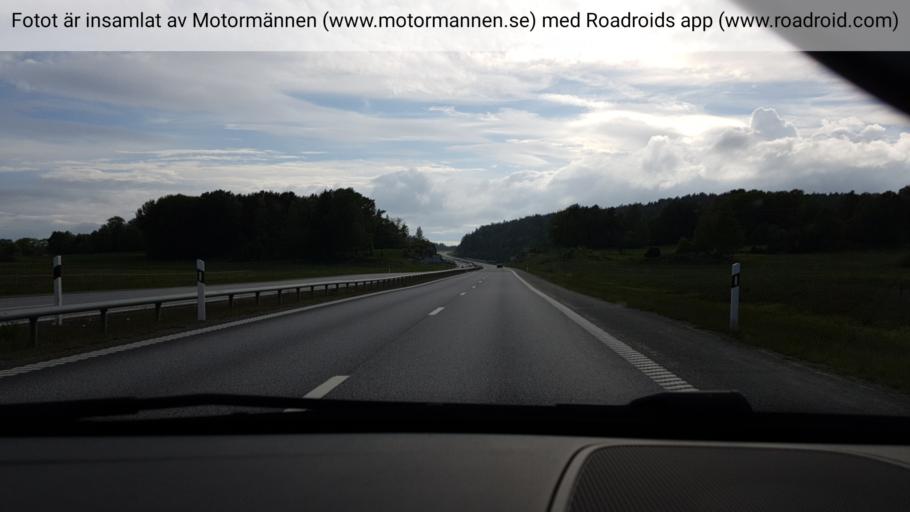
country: SE
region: Stockholm
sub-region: Haninge Kommun
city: Jordbro
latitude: 59.0639
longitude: 18.0516
